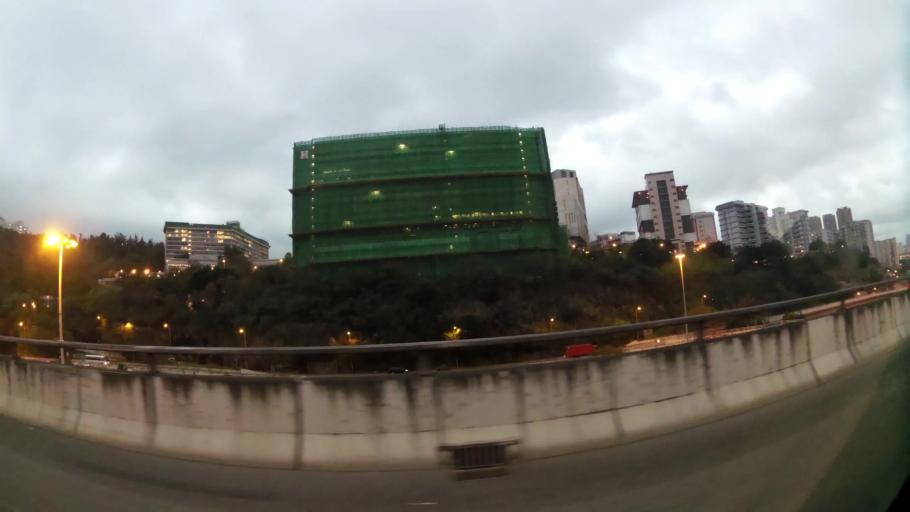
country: HK
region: Sham Shui Po
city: Sham Shui Po
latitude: 22.3407
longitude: 114.1311
